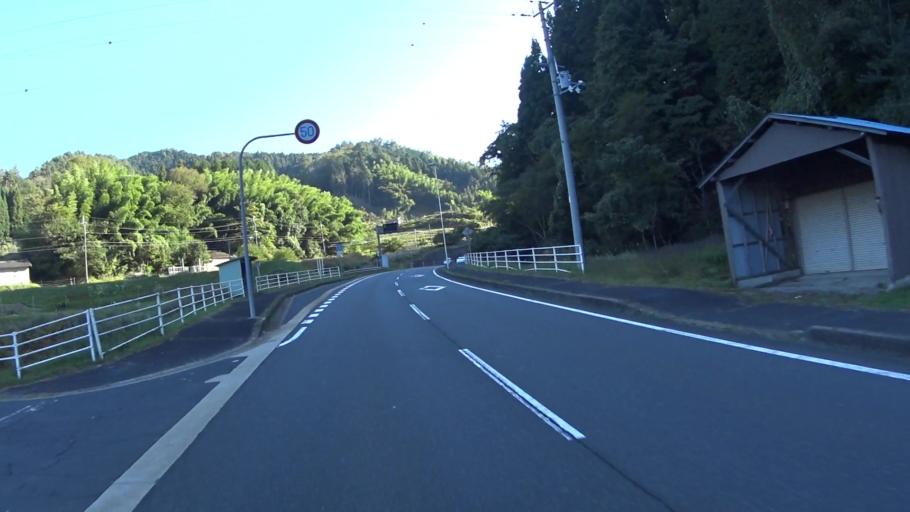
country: JP
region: Kyoto
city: Fukuchiyama
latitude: 35.4156
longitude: 135.0865
